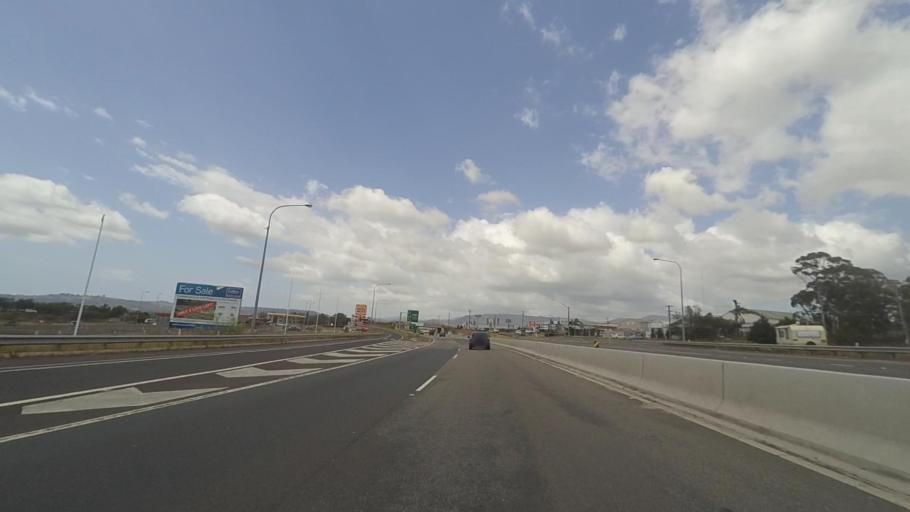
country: AU
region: New South Wales
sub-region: Shellharbour
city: Albion Park Rail
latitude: -34.5392
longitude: 150.7848
